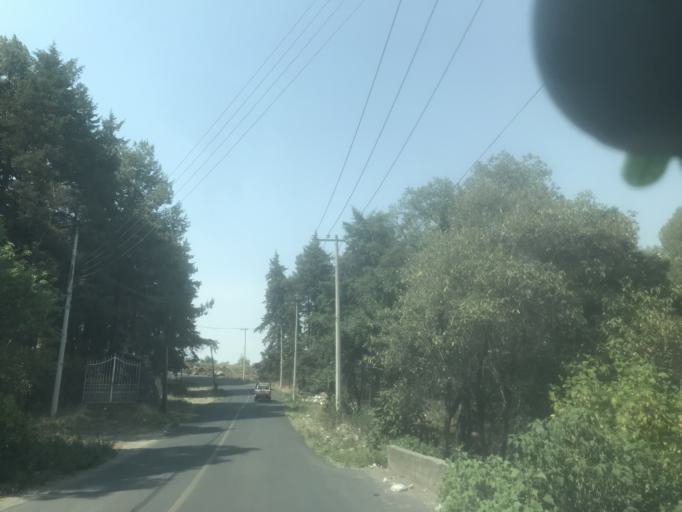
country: MX
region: Mexico
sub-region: Atlautla
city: San Juan Tepecoculco
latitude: 18.9932
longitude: -98.7940
